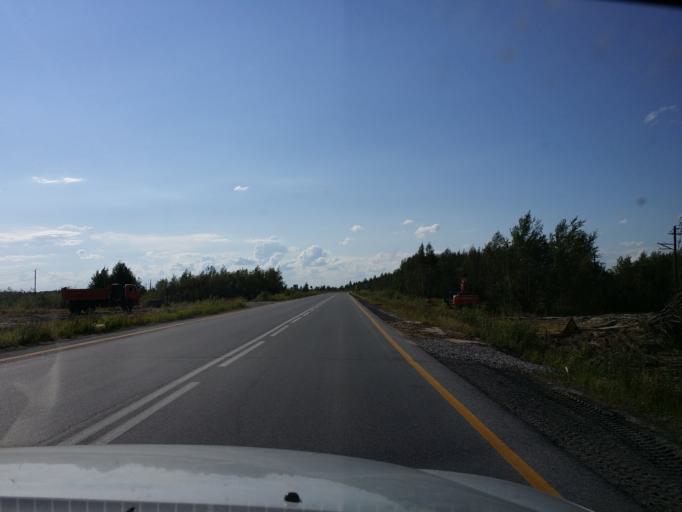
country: RU
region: Khanty-Mansiyskiy Avtonomnyy Okrug
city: Lokosovo
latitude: 61.3942
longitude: 74.8735
